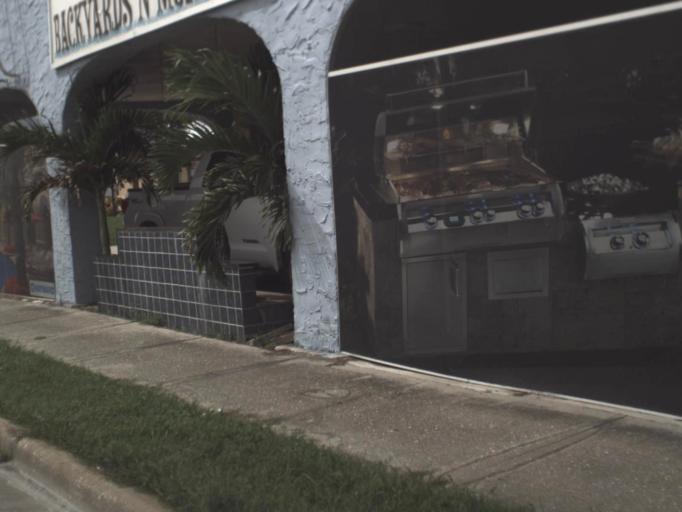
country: US
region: Florida
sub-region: Manatee County
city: Ellenton
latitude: 27.5219
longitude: -82.5243
